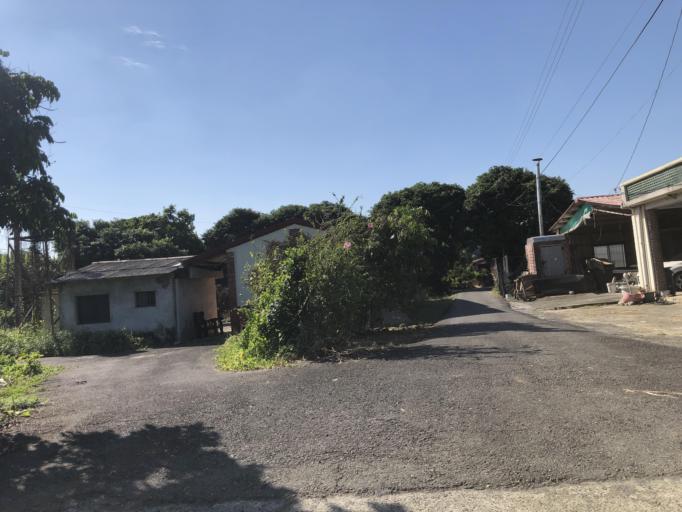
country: TW
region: Taiwan
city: Yujing
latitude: 23.0474
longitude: 120.4009
